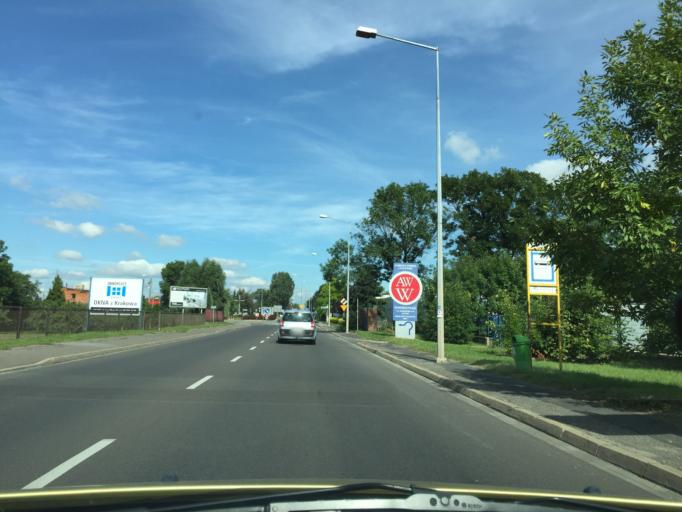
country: PL
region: Greater Poland Voivodeship
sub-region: Kalisz
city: Kalisz
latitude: 51.7825
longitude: 18.0897
